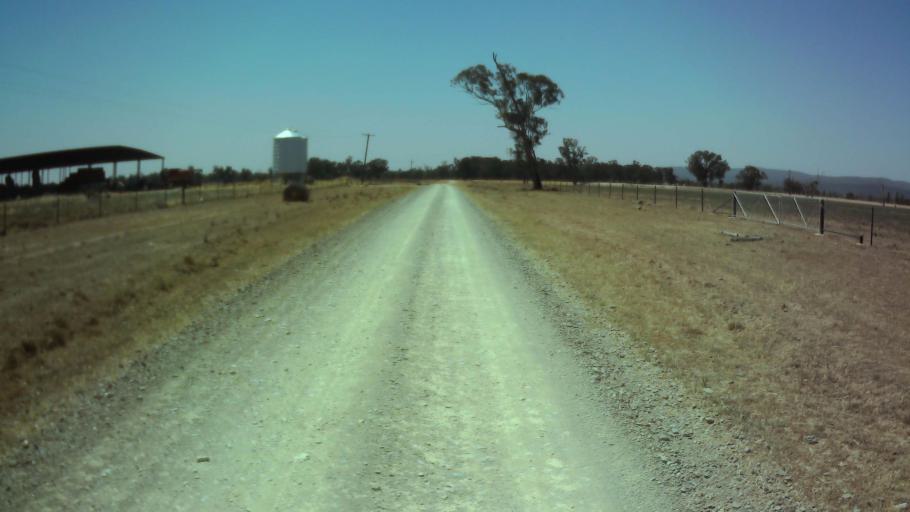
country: AU
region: New South Wales
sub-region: Weddin
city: Grenfell
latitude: -34.0261
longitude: 147.9000
